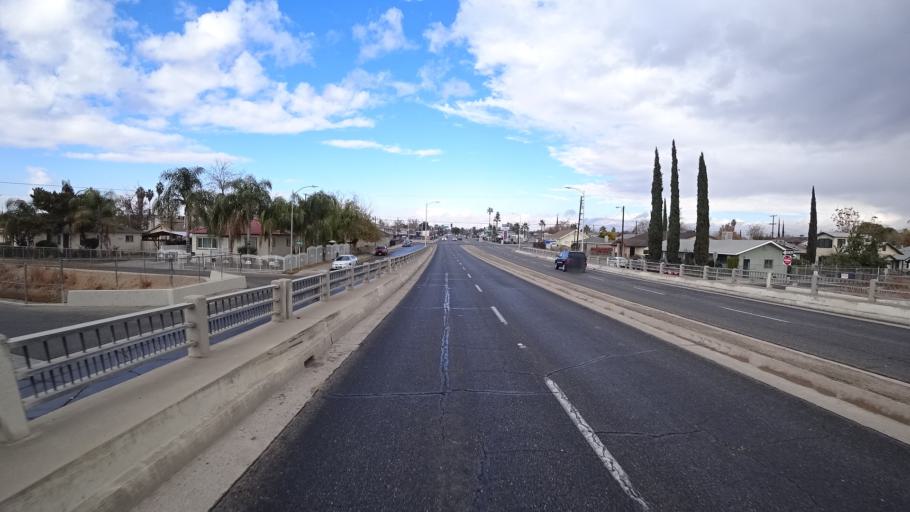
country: US
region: California
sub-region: Kern County
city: Bakersfield
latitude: 35.3790
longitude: -118.9888
